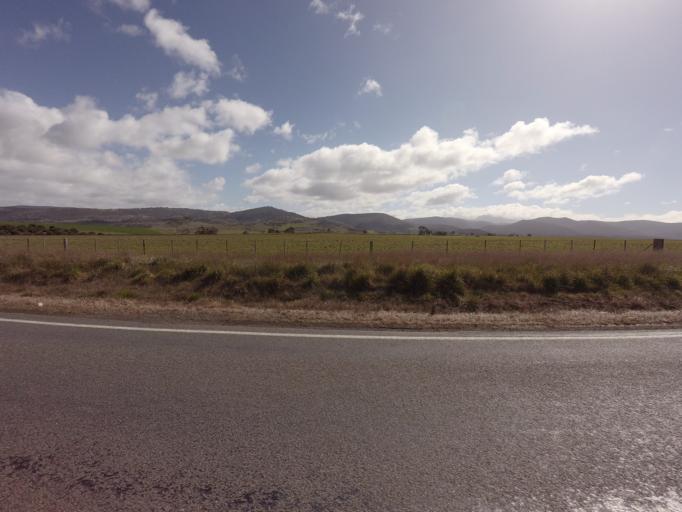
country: AU
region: Tasmania
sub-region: Northern Midlands
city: Evandale
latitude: -41.7969
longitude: 147.7060
